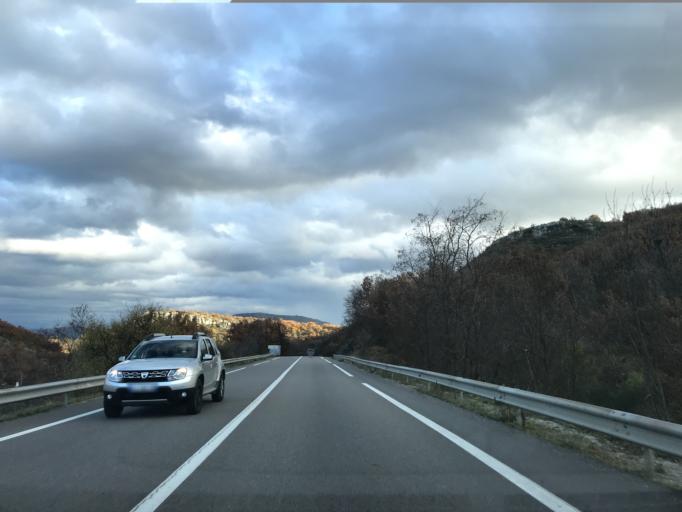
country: FR
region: Rhone-Alpes
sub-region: Departement de l'Ardeche
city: Alissas
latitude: 44.7134
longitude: 4.6166
